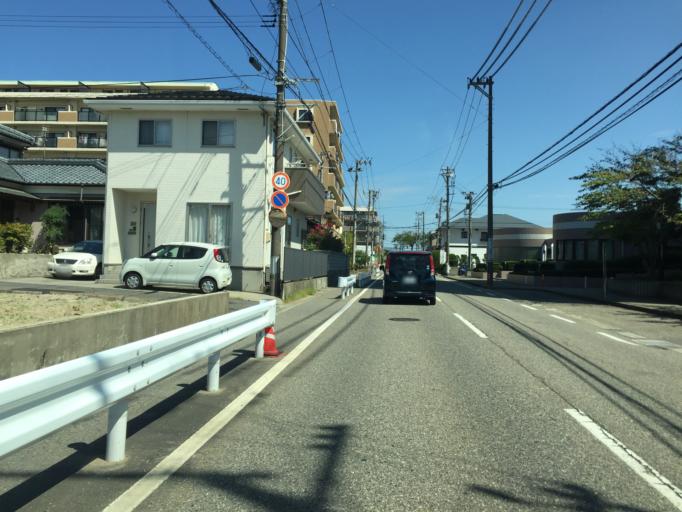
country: JP
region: Niigata
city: Niigata-shi
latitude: 37.8979
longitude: 139.0060
